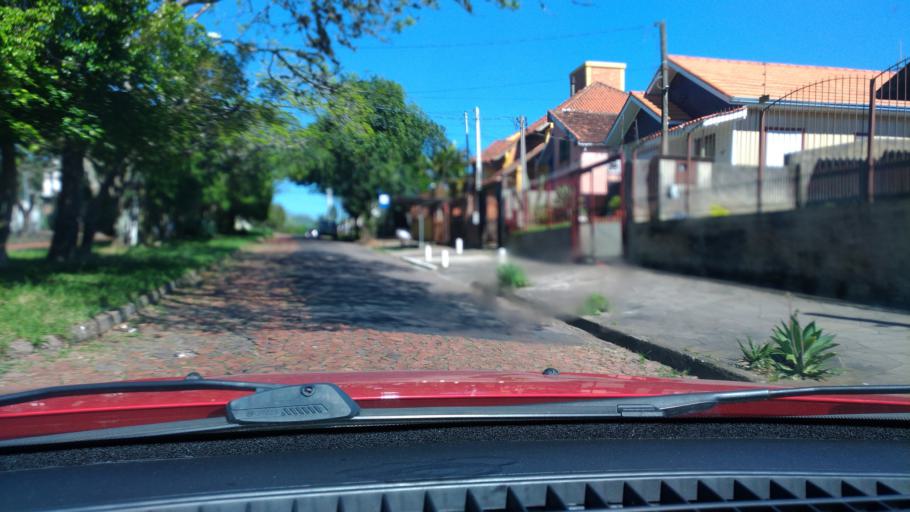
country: BR
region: Rio Grande do Sul
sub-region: Cachoeirinha
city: Cachoeirinha
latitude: -30.0333
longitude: -51.1332
